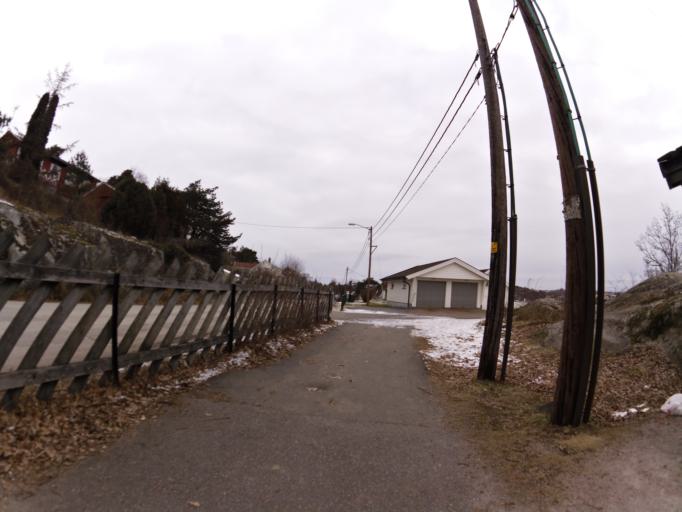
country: NO
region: Ostfold
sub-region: Fredrikstad
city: Fredrikstad
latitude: 59.2083
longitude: 10.8859
